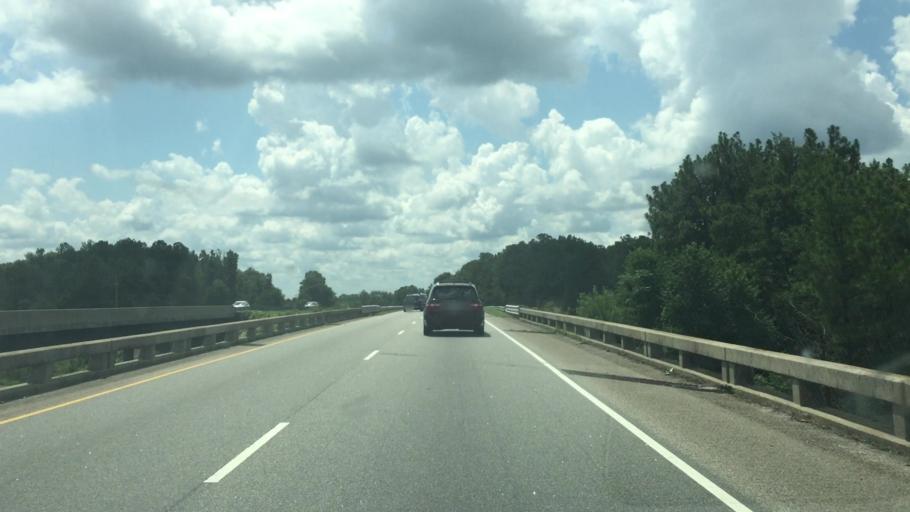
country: US
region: North Carolina
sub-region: Scotland County
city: Laurel Hill
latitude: 34.8329
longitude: -79.5952
